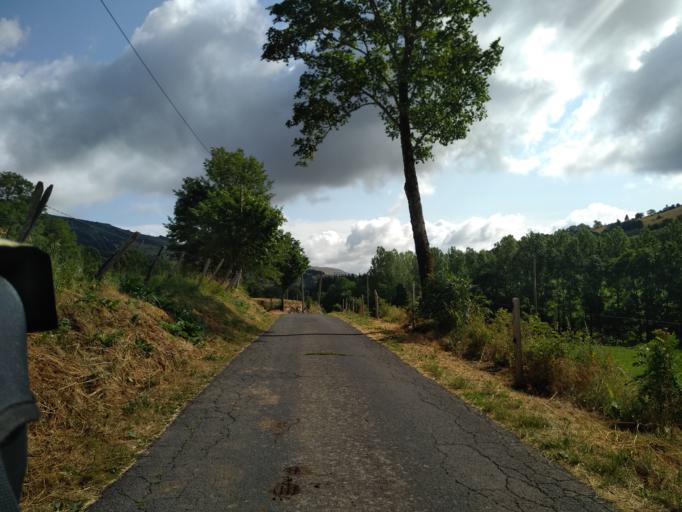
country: FR
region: Auvergne
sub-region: Departement du Cantal
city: Murat
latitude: 45.1271
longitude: 2.7402
